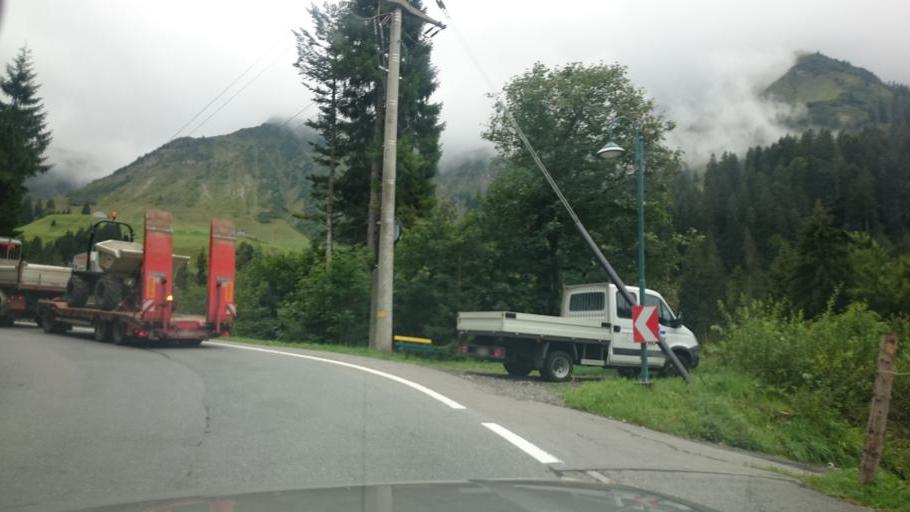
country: AT
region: Vorarlberg
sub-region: Politischer Bezirk Bregenz
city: Schroecken
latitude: 47.2588
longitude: 10.0904
